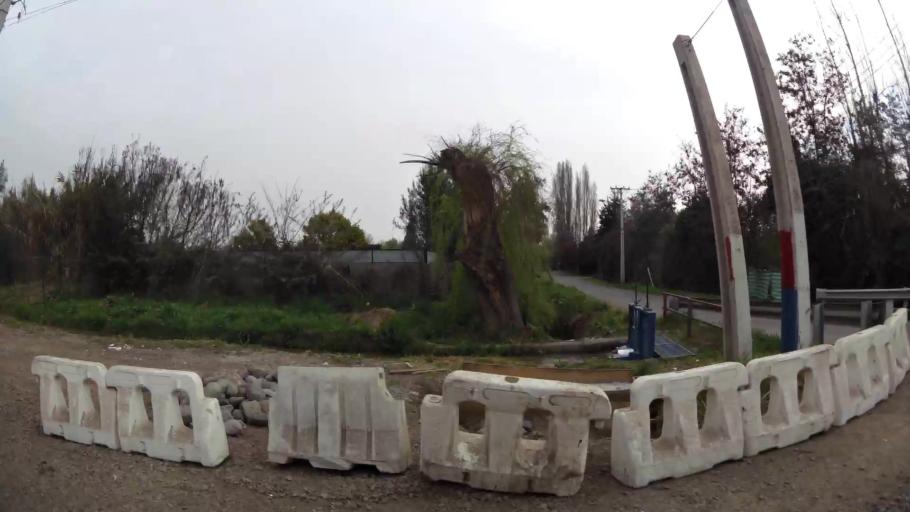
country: CL
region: Santiago Metropolitan
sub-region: Provincia de Chacabuco
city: Chicureo Abajo
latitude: -33.2685
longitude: -70.7170
